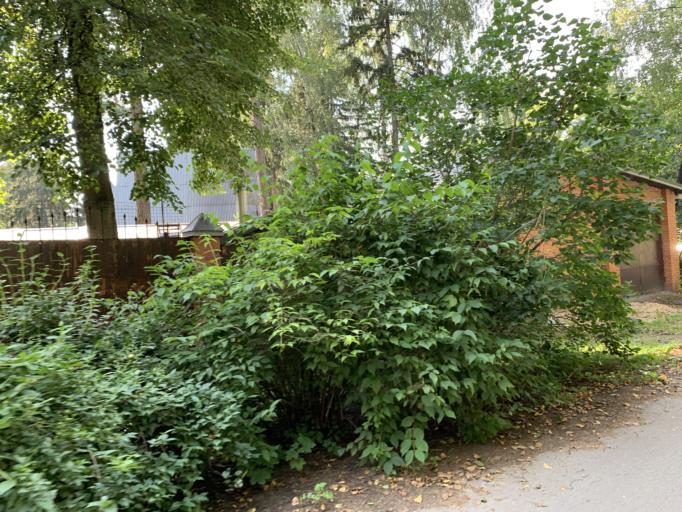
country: RU
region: Moskovskaya
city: Mamontovka
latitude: 55.9748
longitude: 37.8249
